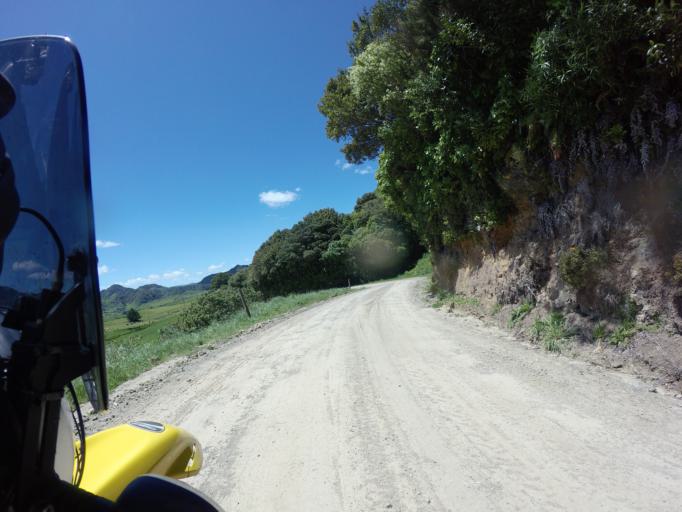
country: NZ
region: Bay of Plenty
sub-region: Opotiki District
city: Opotiki
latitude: -38.4055
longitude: 177.4486
